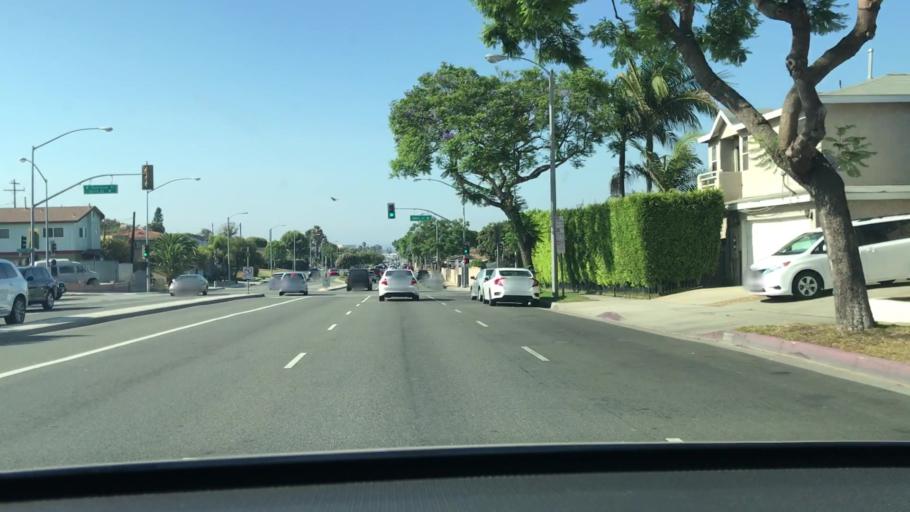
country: US
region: California
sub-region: Los Angeles County
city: Lawndale
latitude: 33.8796
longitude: -118.3612
